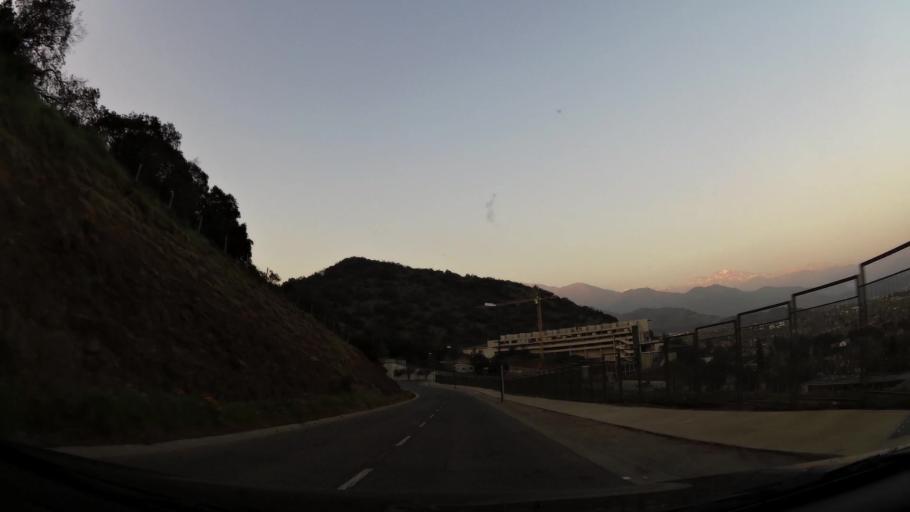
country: CL
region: Santiago Metropolitan
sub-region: Provincia de Chacabuco
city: Chicureo Abajo
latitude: -33.3325
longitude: -70.5557
